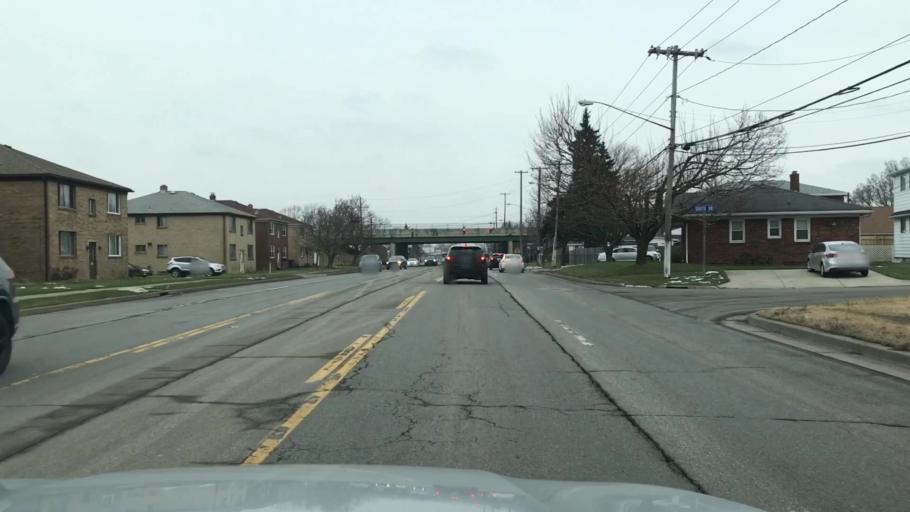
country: US
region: New York
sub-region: Erie County
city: Blasdell
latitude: 42.8095
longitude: -78.7988
